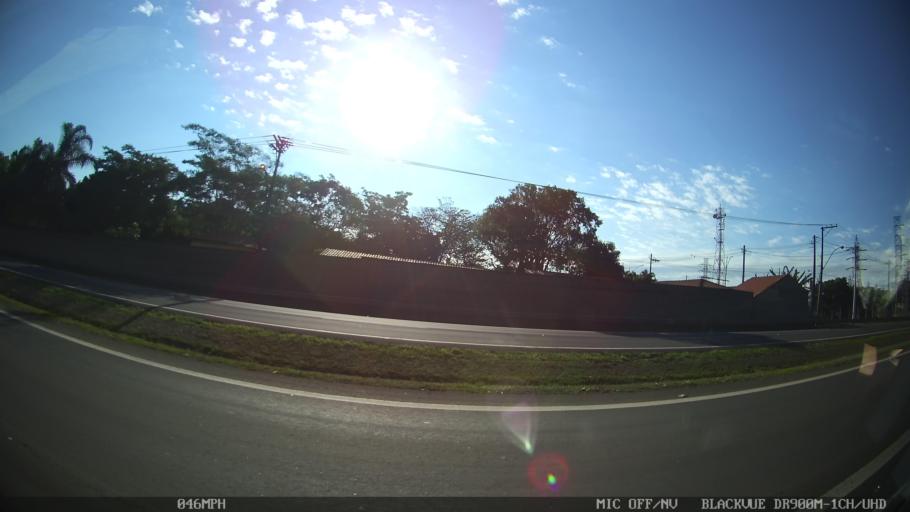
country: BR
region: Sao Paulo
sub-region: Piracicaba
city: Piracicaba
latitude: -22.6953
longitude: -47.6502
